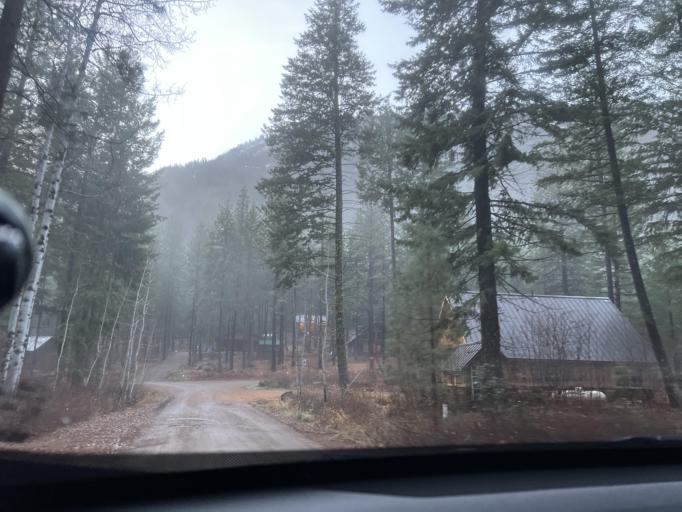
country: US
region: Washington
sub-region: Chelan County
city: Granite Falls
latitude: 48.5579
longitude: -120.3671
